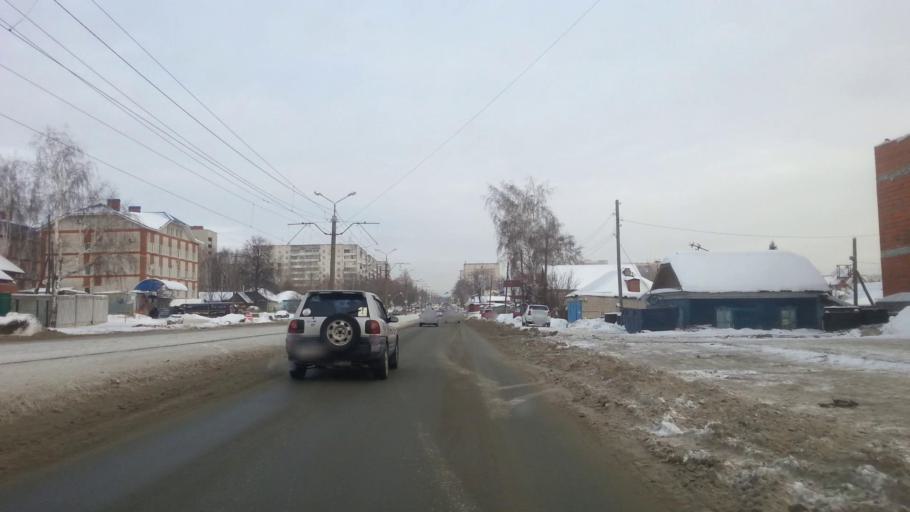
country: RU
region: Altai Krai
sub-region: Gorod Barnaulskiy
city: Barnaul
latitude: 53.3675
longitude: 83.7350
